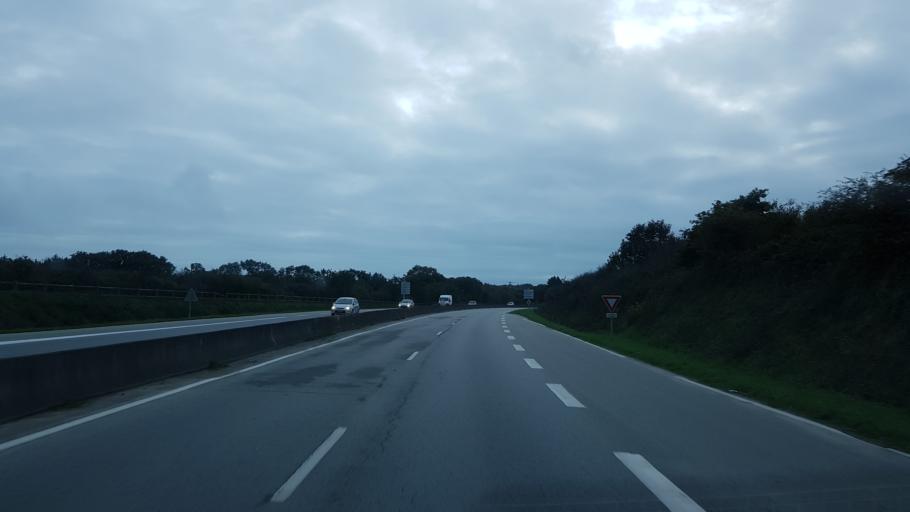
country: FR
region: Brittany
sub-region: Departement du Morbihan
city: Sarzeau
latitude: 47.5465
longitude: -2.7202
